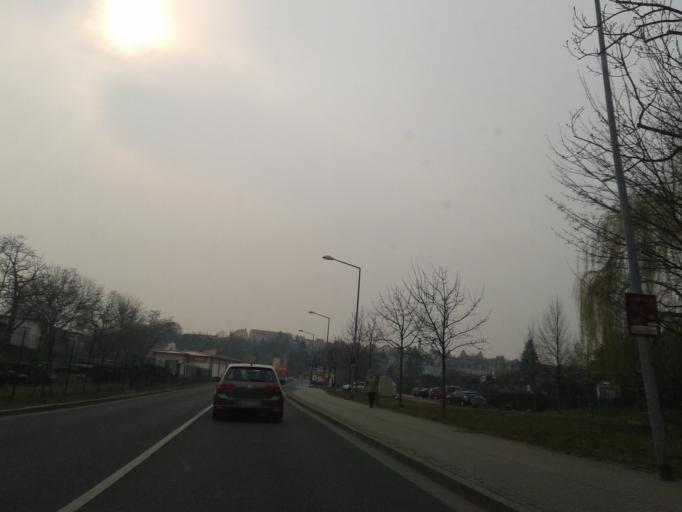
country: DE
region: Saxony
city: Freital
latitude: 51.0162
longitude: 13.6663
